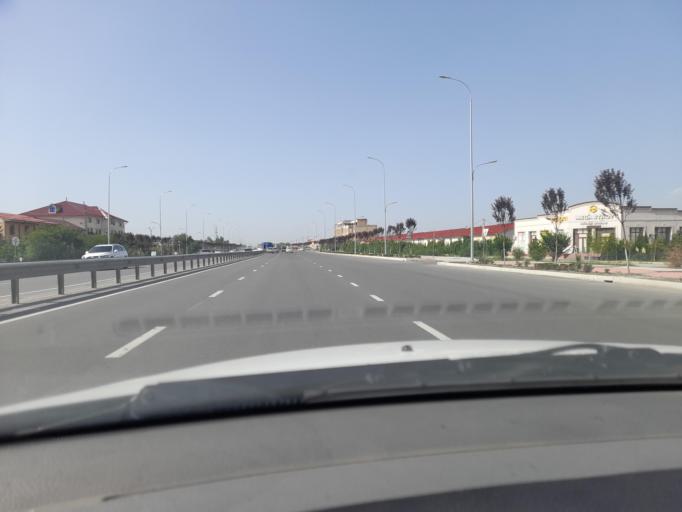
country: UZ
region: Samarqand
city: Samarqand
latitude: 39.7128
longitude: 66.9497
